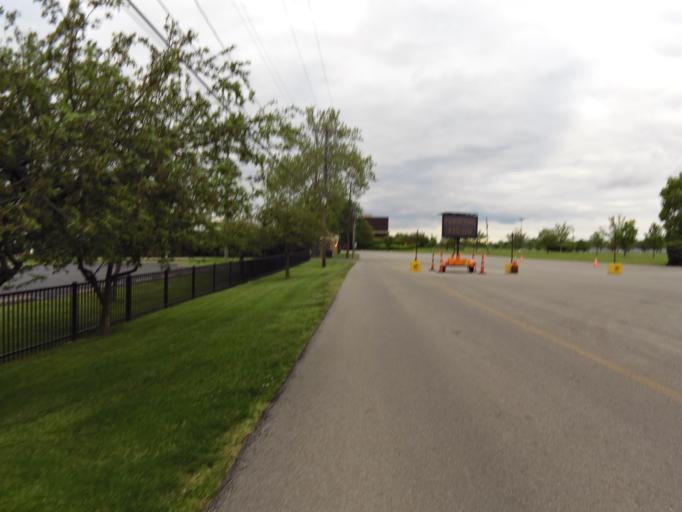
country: US
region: Ohio
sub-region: Franklin County
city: Columbus
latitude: 40.0015
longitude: -82.9876
